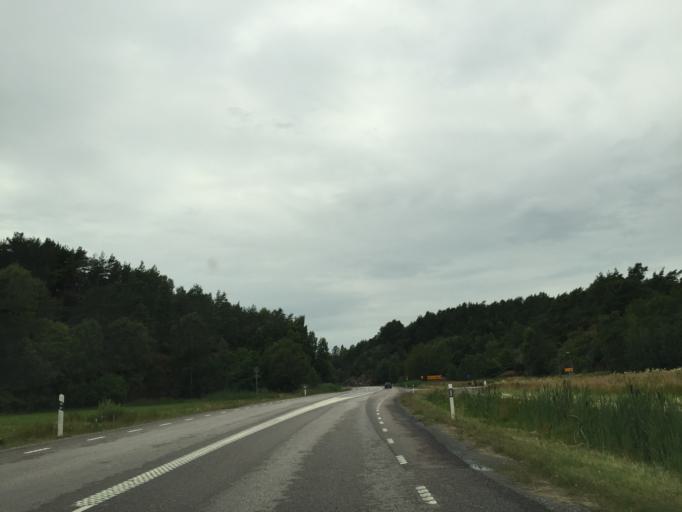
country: SE
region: Vaestra Goetaland
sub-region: Tjorns Kommun
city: Myggenas
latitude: 58.0241
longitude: 11.6784
